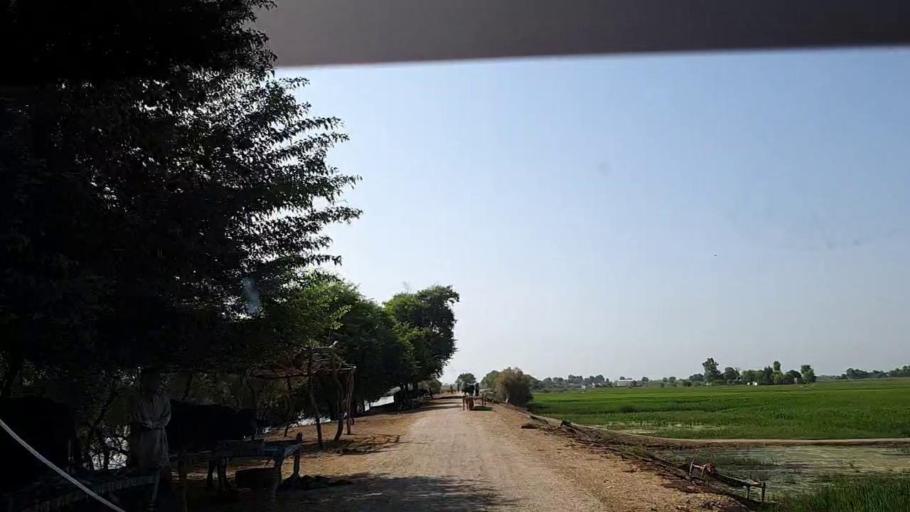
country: PK
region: Sindh
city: Ghauspur
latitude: 28.1945
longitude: 69.0507
